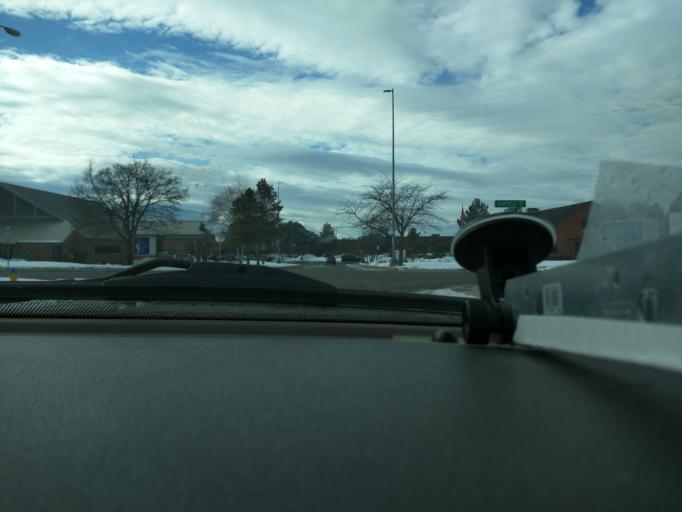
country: US
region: Montana
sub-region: Missoula County
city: Orchard Homes
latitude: 46.8471
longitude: -114.0234
